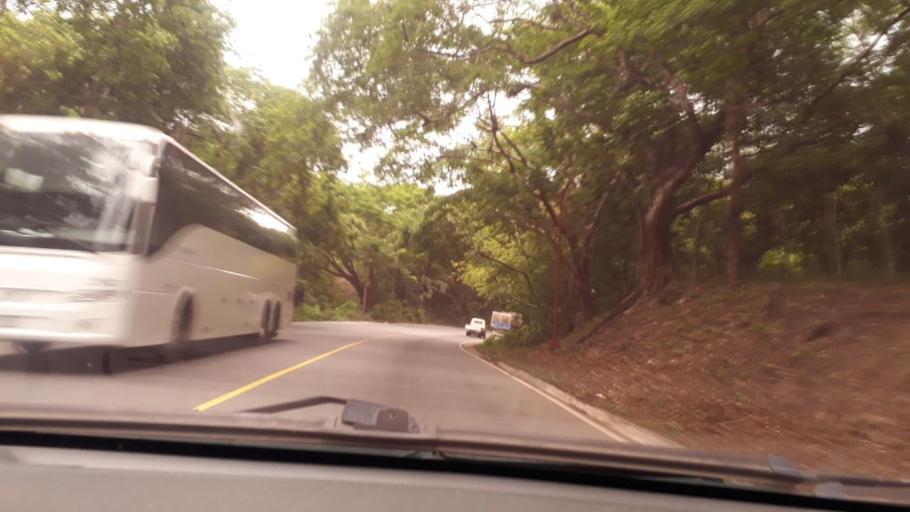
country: GT
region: Izabal
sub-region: Municipio de Los Amates
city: Los Amates
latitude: 15.2319
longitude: -89.2101
